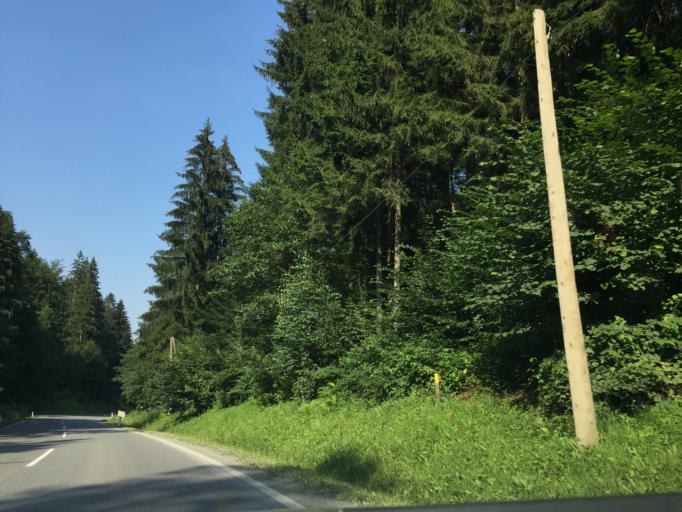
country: AT
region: Styria
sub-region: Politischer Bezirk Deutschlandsberg
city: Aibl
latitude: 46.6526
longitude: 15.2120
